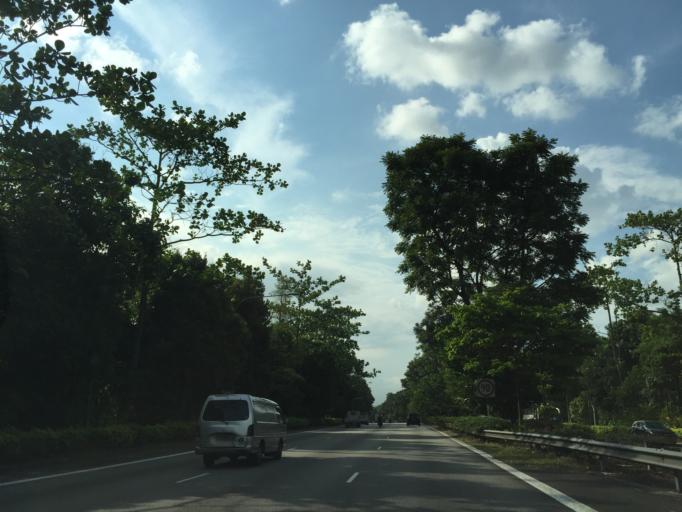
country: MY
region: Johor
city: Johor Bahru
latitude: 1.3669
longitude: 103.7793
